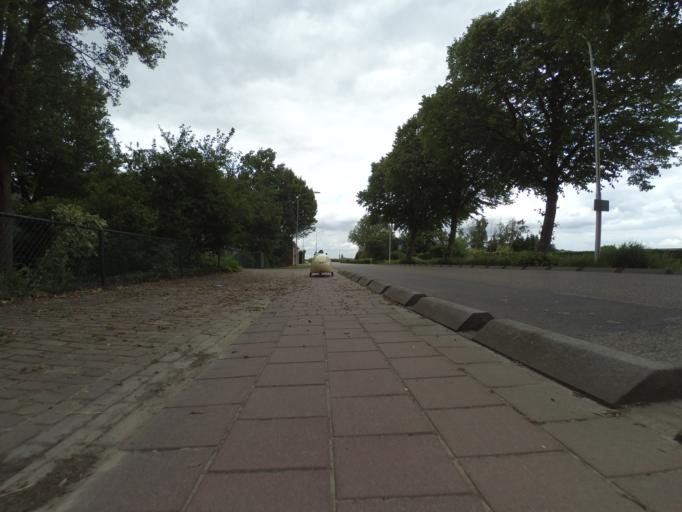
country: NL
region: North Brabant
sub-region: Gemeente Steenbergen
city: Kruisland
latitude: 51.5751
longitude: 4.4172
